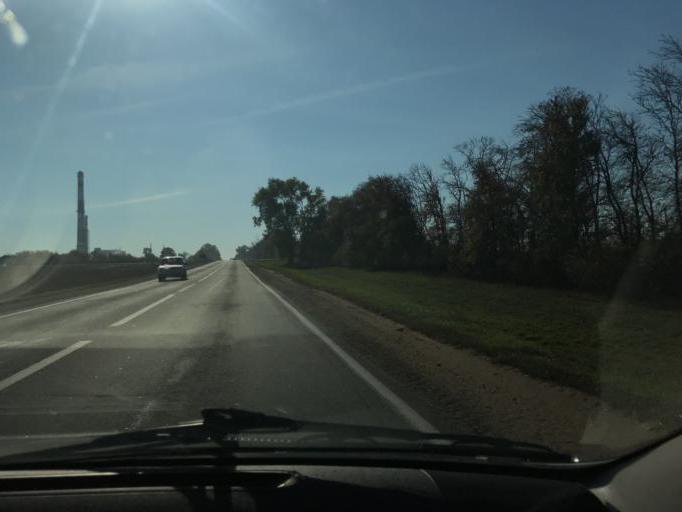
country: BY
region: Minsk
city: Starobin
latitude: 52.8023
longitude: 27.4647
